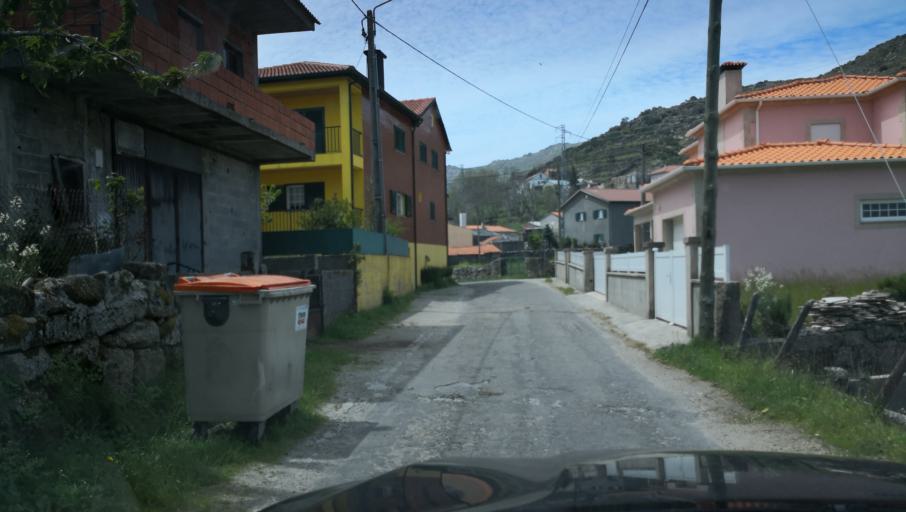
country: PT
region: Vila Real
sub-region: Vila Real
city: Vila Real
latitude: 41.3244
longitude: -7.8038
